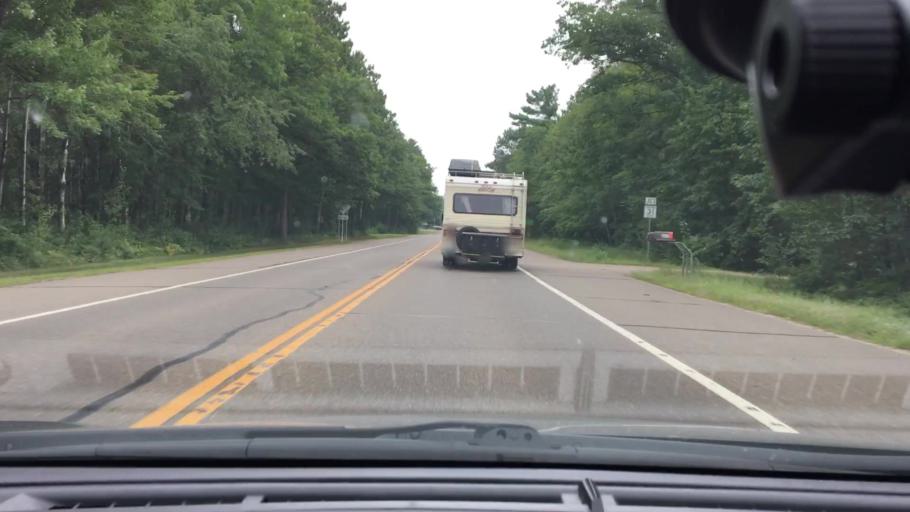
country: US
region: Minnesota
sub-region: Crow Wing County
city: Crosby
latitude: 46.4832
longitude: -93.9405
